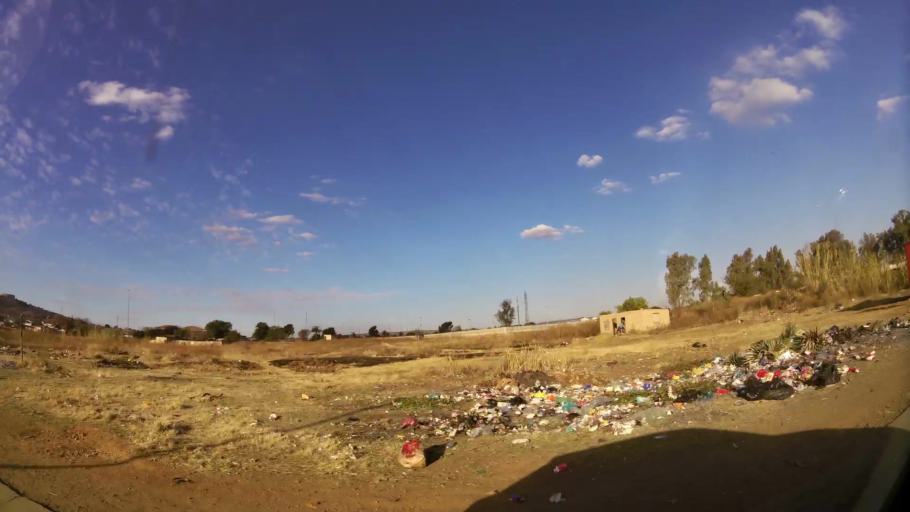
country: ZA
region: Gauteng
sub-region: City of Tshwane Metropolitan Municipality
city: Cullinan
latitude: -25.7101
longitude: 28.3742
